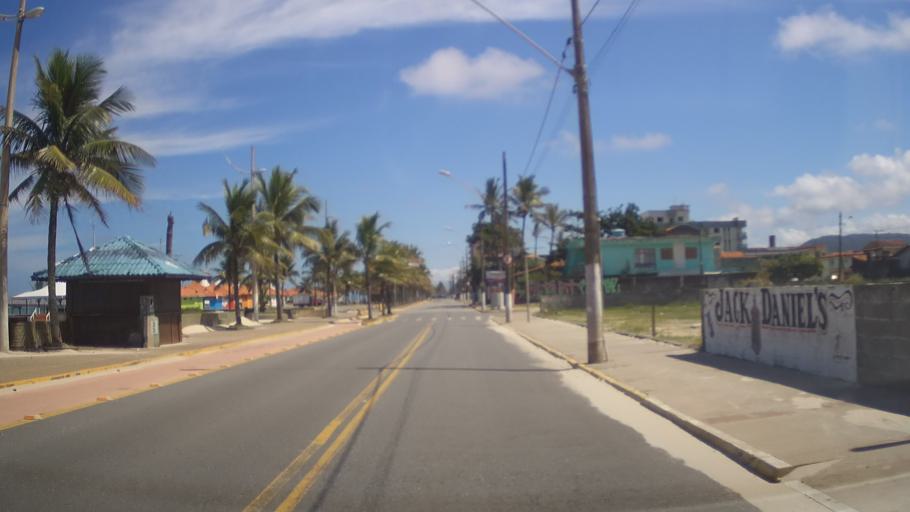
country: BR
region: Sao Paulo
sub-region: Mongagua
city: Mongagua
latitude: -24.1323
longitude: -46.6909
